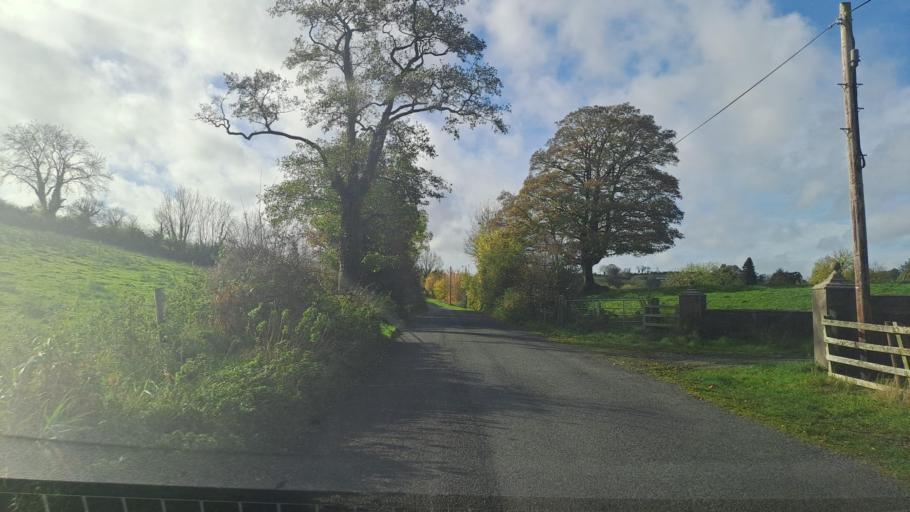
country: IE
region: Ulster
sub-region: An Cabhan
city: Cootehill
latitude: 54.0343
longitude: -7.0136
